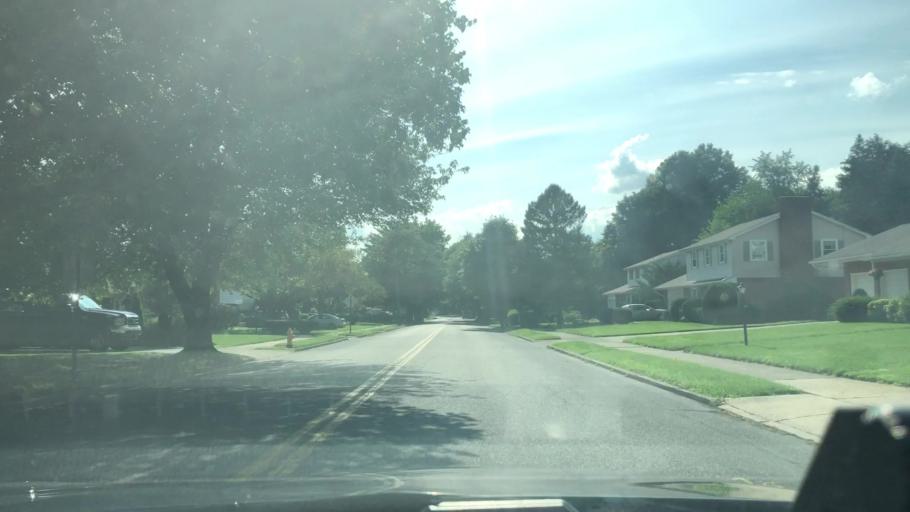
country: US
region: Pennsylvania
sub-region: Lehigh County
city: Fountain Hill
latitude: 40.6387
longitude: -75.4145
